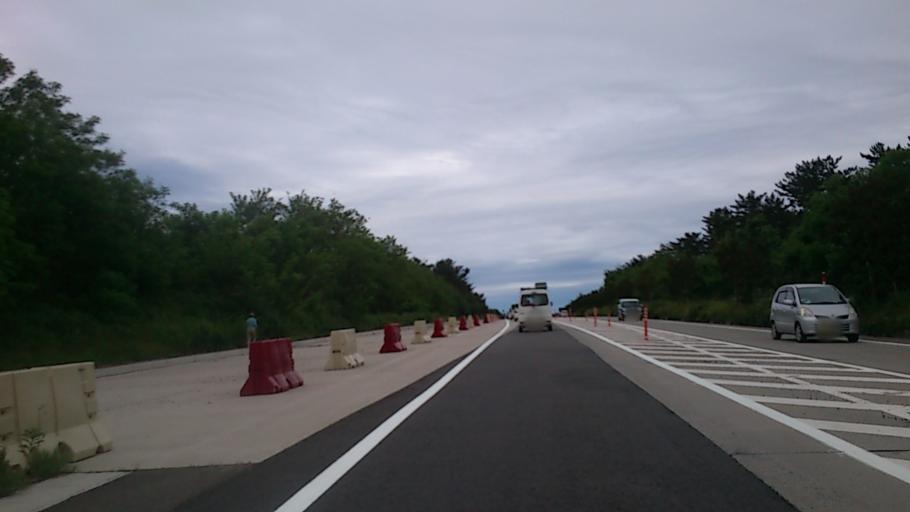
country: JP
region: Akita
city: Akita Shi
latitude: 39.7084
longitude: 140.0732
